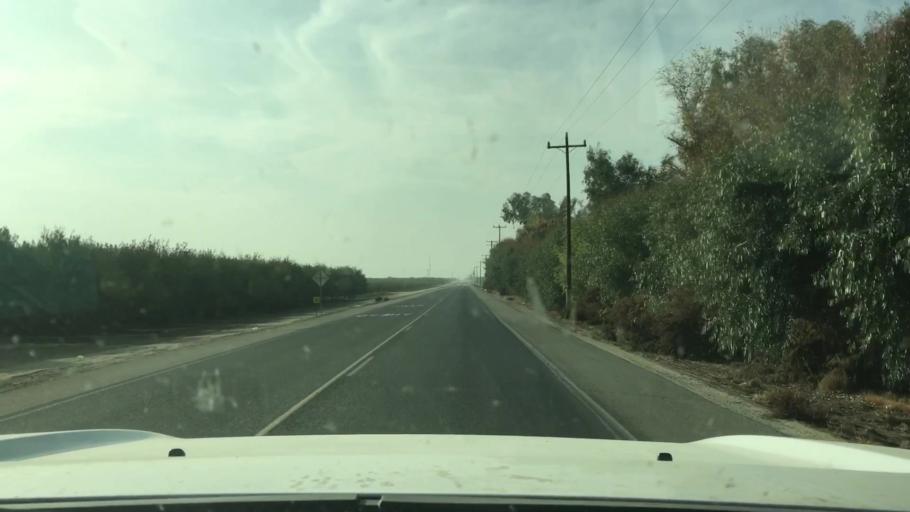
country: US
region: California
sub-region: Kern County
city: Buttonwillow
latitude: 35.5006
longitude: -119.4768
